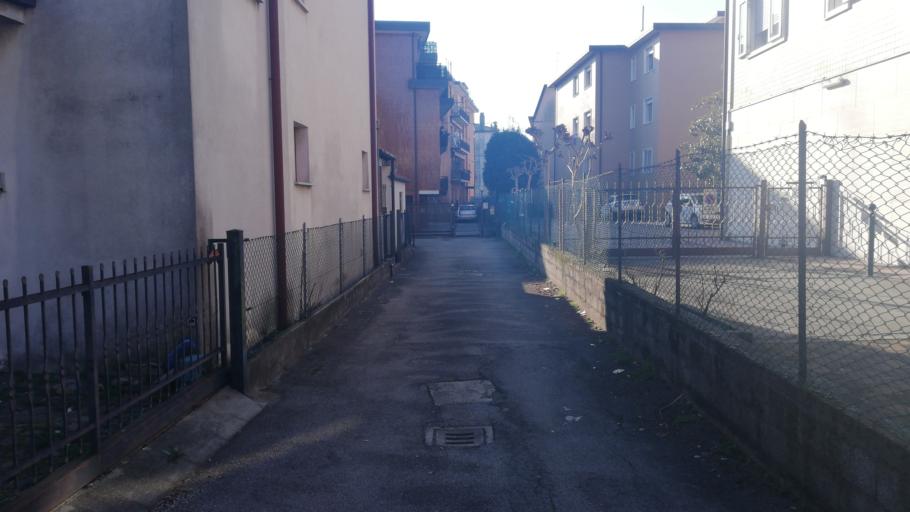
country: IT
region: Veneto
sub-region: Provincia di Venezia
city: Campalto
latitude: 45.5037
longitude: 12.2586
